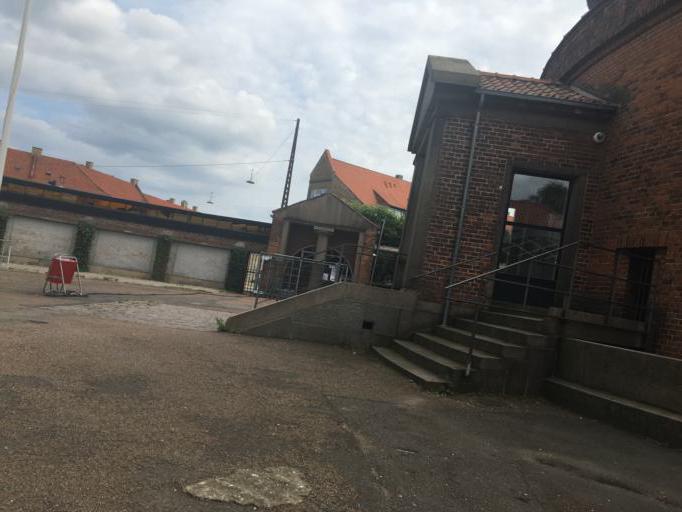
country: DK
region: Capital Region
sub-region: Frederiksberg Kommune
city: Frederiksberg
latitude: 55.7163
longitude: 12.5305
